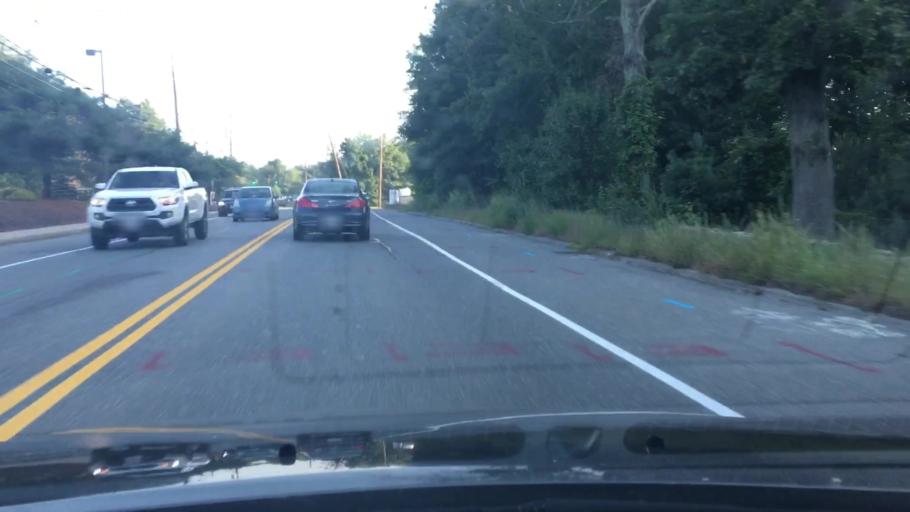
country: US
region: Massachusetts
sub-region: Middlesex County
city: Hopkinton
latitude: 42.2042
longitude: -71.5447
